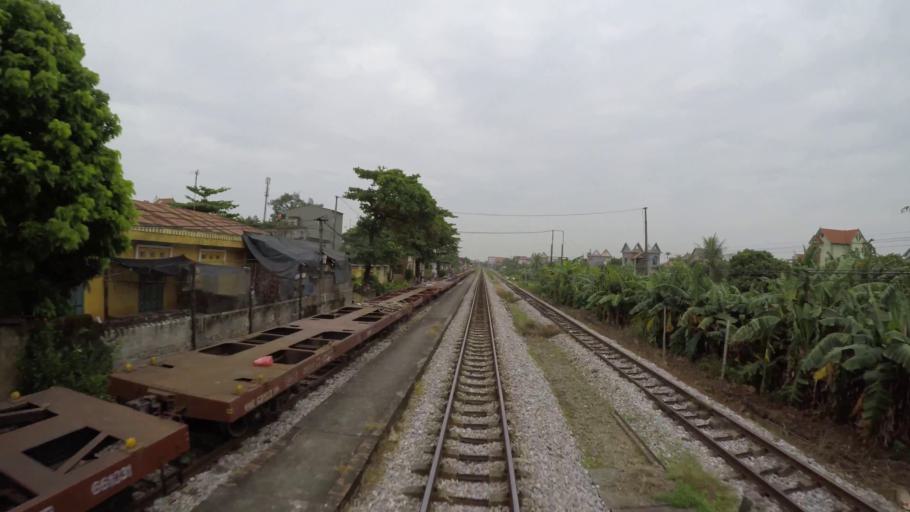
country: VN
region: Hai Duong
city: Phu Thai
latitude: 20.9736
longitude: 106.4378
